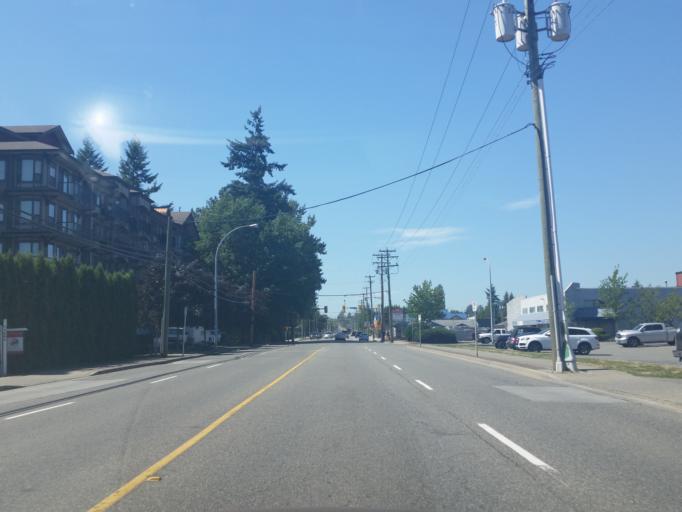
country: CA
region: British Columbia
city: Langley
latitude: 49.1044
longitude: -122.6721
